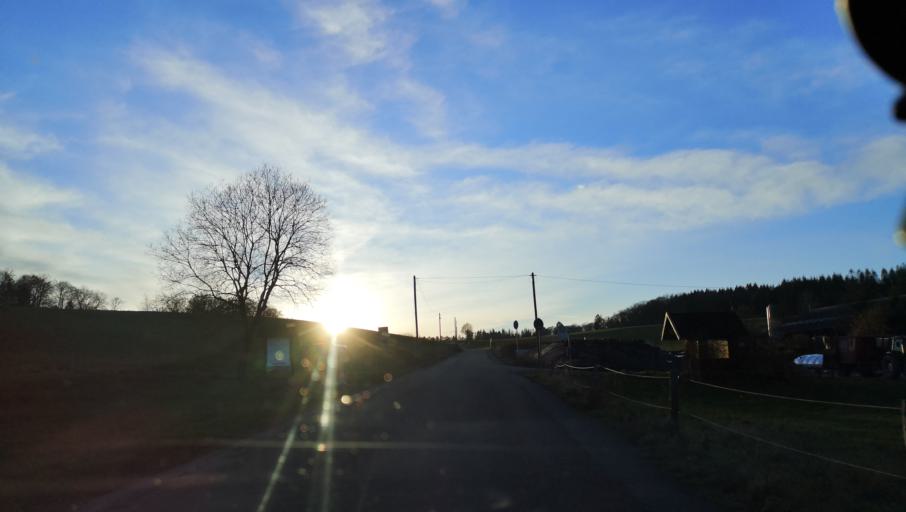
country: DE
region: North Rhine-Westphalia
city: Radevormwald
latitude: 51.1686
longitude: 7.3940
